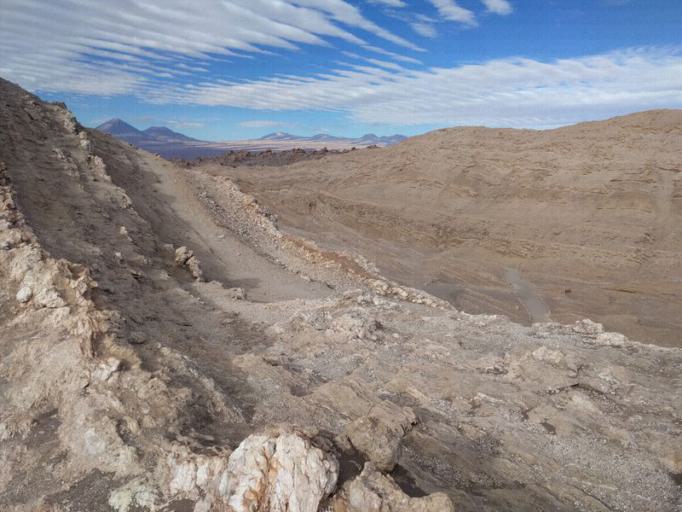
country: CL
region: Antofagasta
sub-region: Provincia de El Loa
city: San Pedro de Atacama
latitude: -22.9488
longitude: -68.2980
